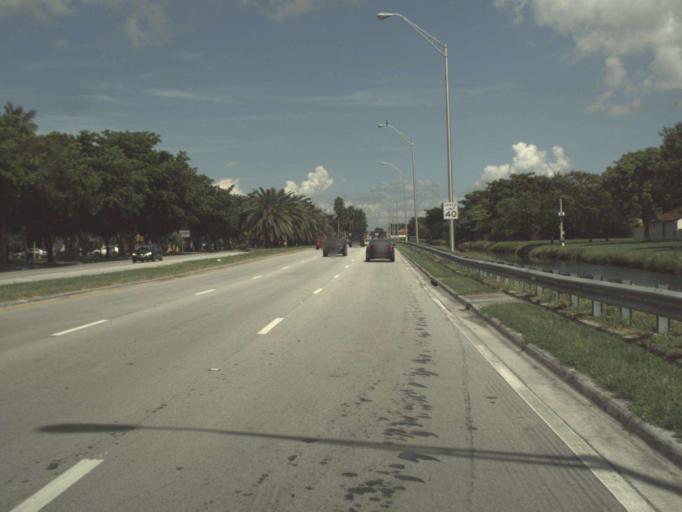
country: US
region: Florida
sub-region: Miami-Dade County
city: The Crossings
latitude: 25.6637
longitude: -80.4160
